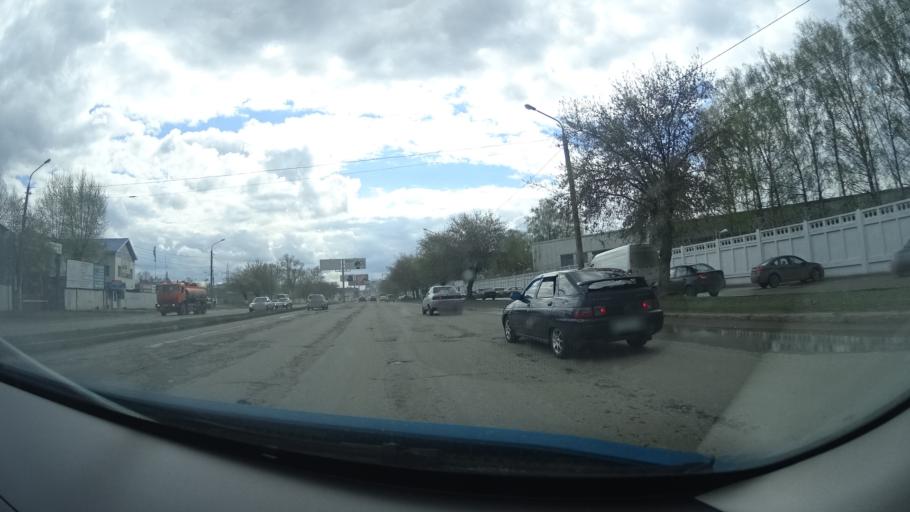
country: RU
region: Bashkortostan
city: Ufa
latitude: 54.8017
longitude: 56.0797
